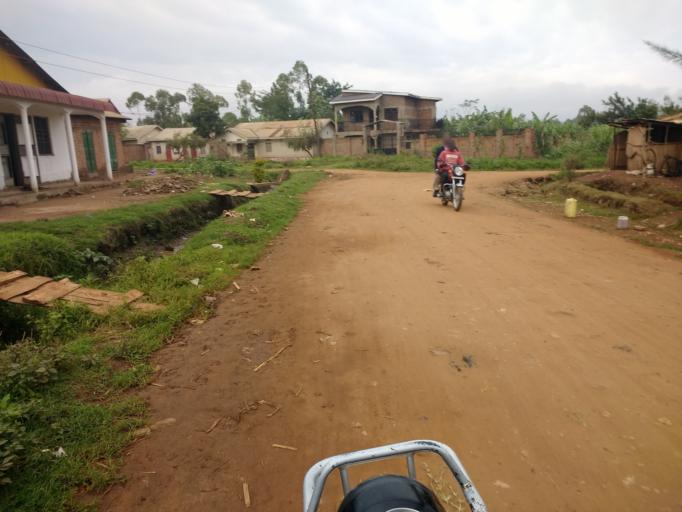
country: UG
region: Eastern Region
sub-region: Mbale District
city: Mbale
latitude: 1.0675
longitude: 34.1594
